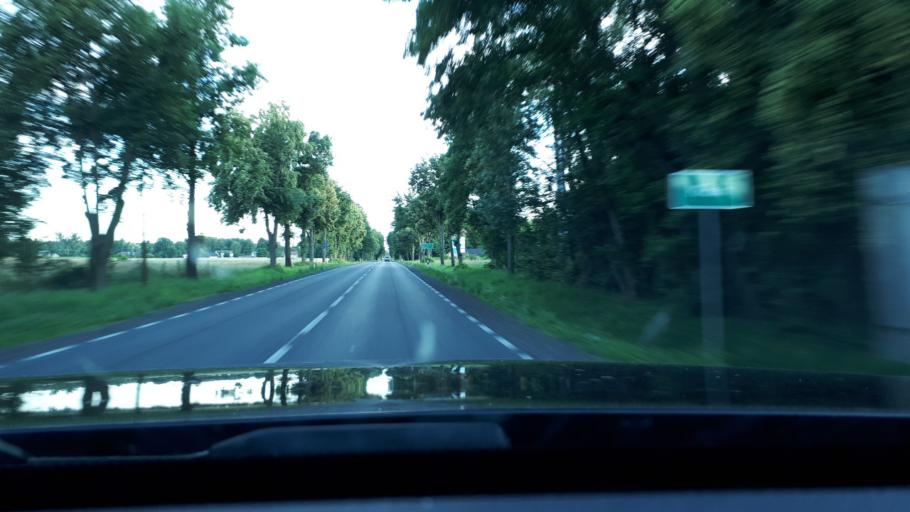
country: PL
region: Masovian Voivodeship
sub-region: Powiat ciechanowski
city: Ojrzen
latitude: 52.7591
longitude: 20.5395
